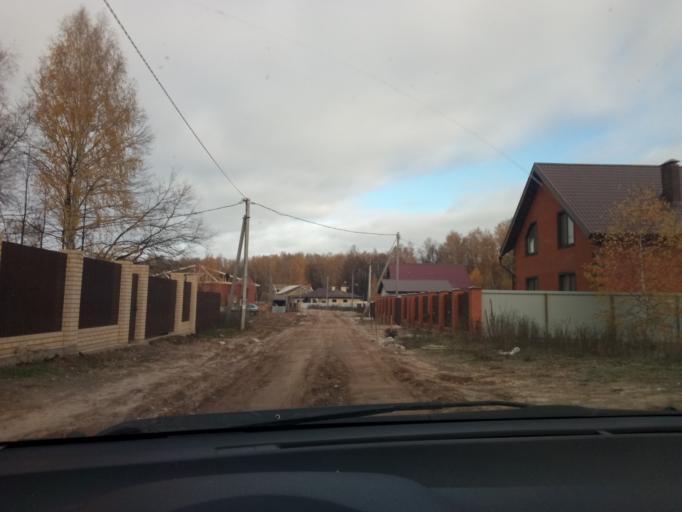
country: RU
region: Tatarstan
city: Staroye Arakchino
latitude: 55.9681
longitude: 49.0452
